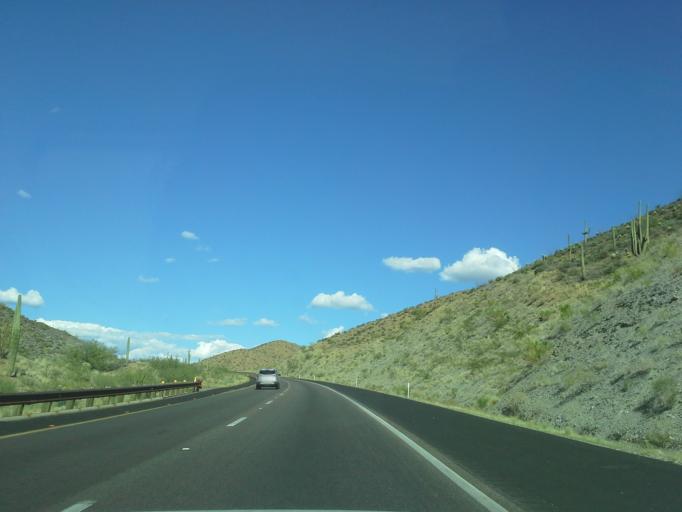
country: US
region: Arizona
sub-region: Pinal County
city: Gold Camp
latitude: 33.2713
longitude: -111.2399
